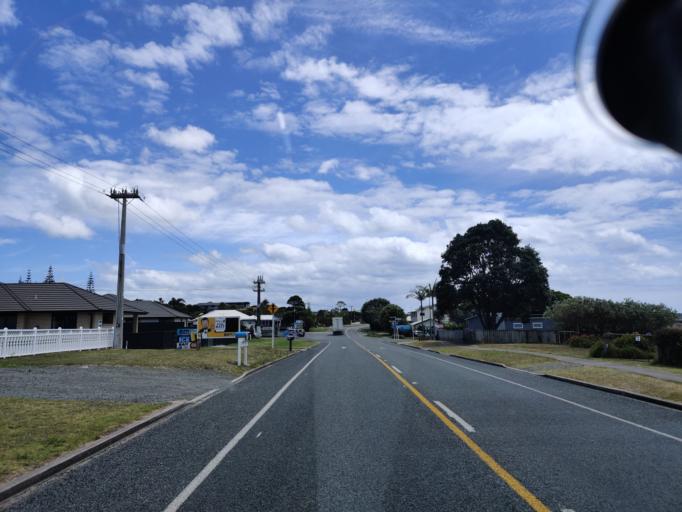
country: NZ
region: Northland
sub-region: Far North District
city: Kaitaia
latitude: -34.8158
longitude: 173.1185
